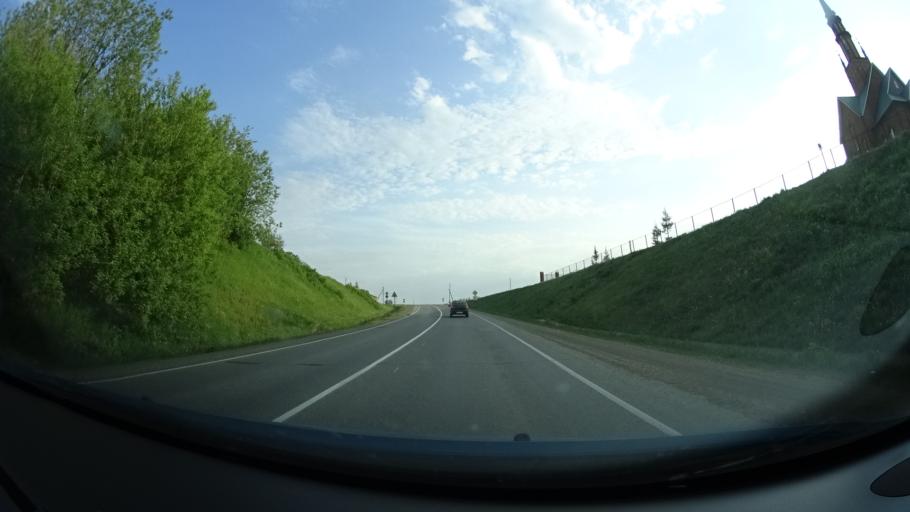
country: RU
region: Perm
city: Barda
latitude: 56.9174
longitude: 55.5924
